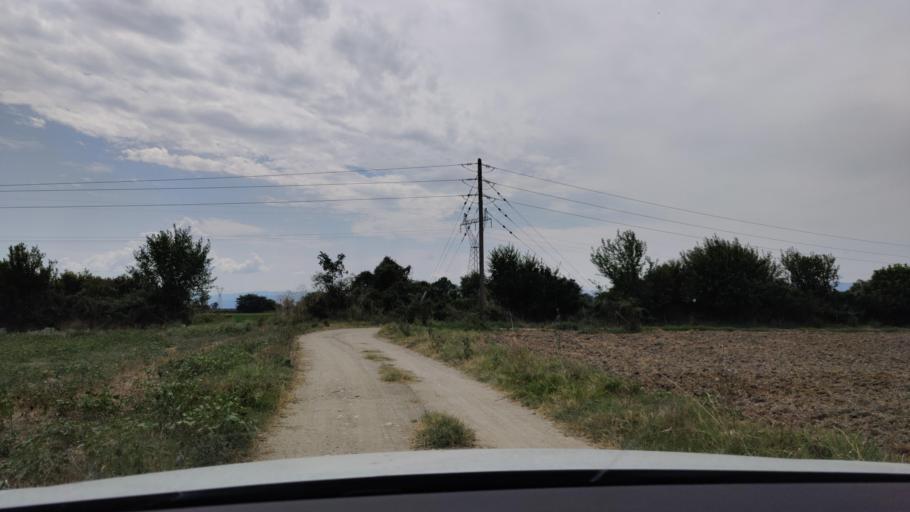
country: GR
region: Central Macedonia
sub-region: Nomos Serron
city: Serres
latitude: 41.0584
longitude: 23.5432
